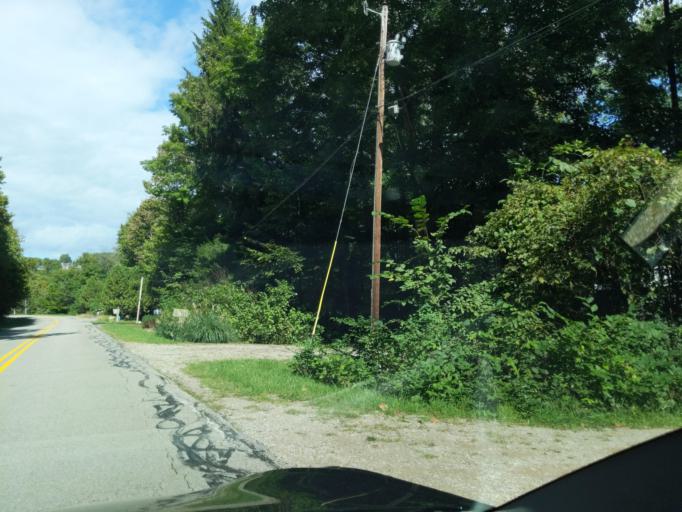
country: US
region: Michigan
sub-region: Antrim County
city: Elk Rapids
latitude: 44.9564
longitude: -85.3231
